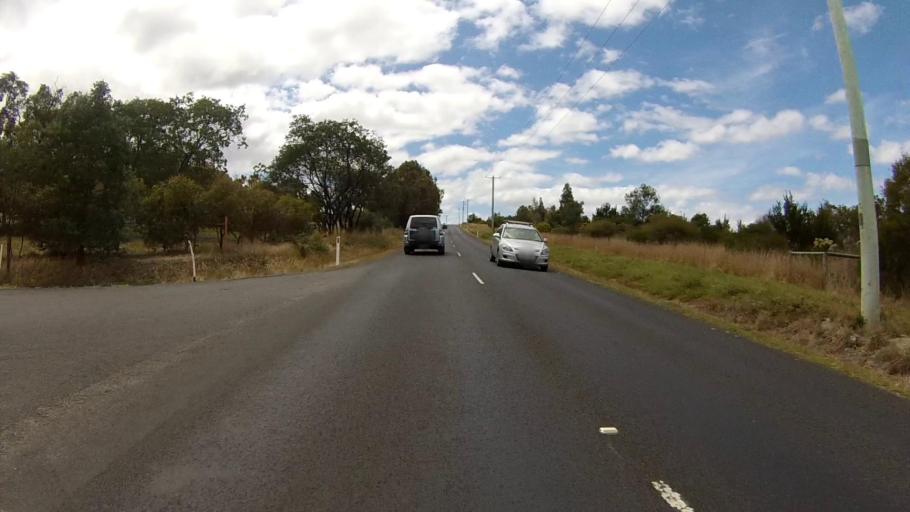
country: AU
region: Tasmania
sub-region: Sorell
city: Sorell
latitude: -42.8169
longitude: 147.6125
